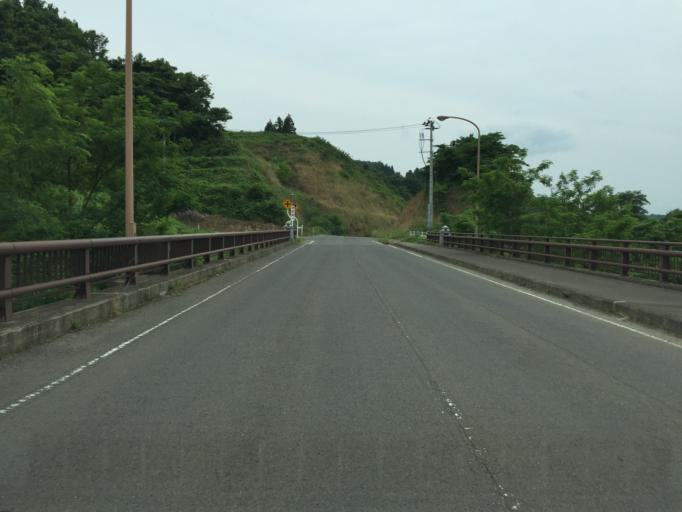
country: JP
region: Fukushima
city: Nihommatsu
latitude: 37.6470
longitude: 140.5266
